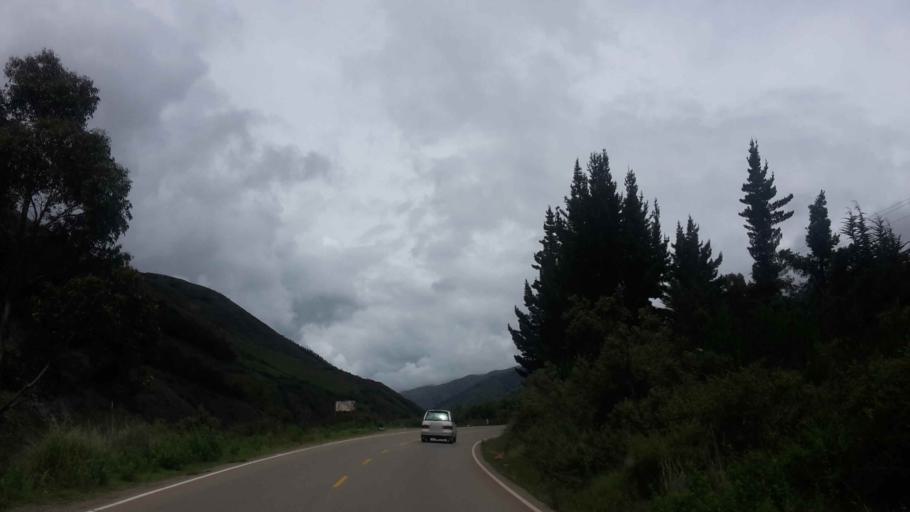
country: BO
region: Cochabamba
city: Totora
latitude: -17.5287
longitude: -65.3841
